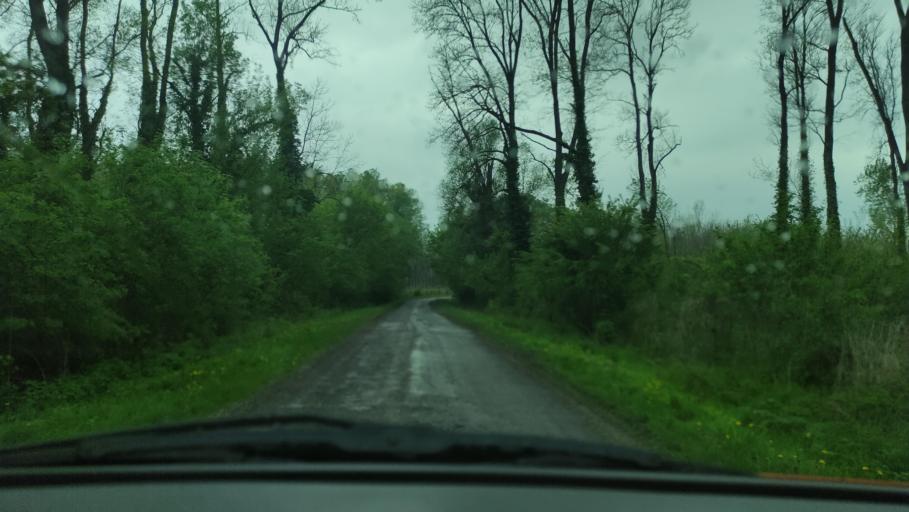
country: HU
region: Baranya
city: Mohacs
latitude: 45.9094
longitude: 18.7556
